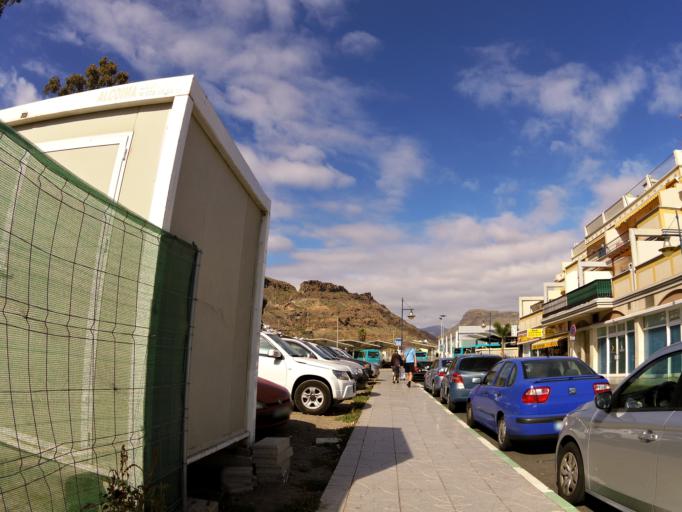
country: ES
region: Canary Islands
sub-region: Provincia de Las Palmas
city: Puerto Rico
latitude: 27.8200
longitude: -15.7628
